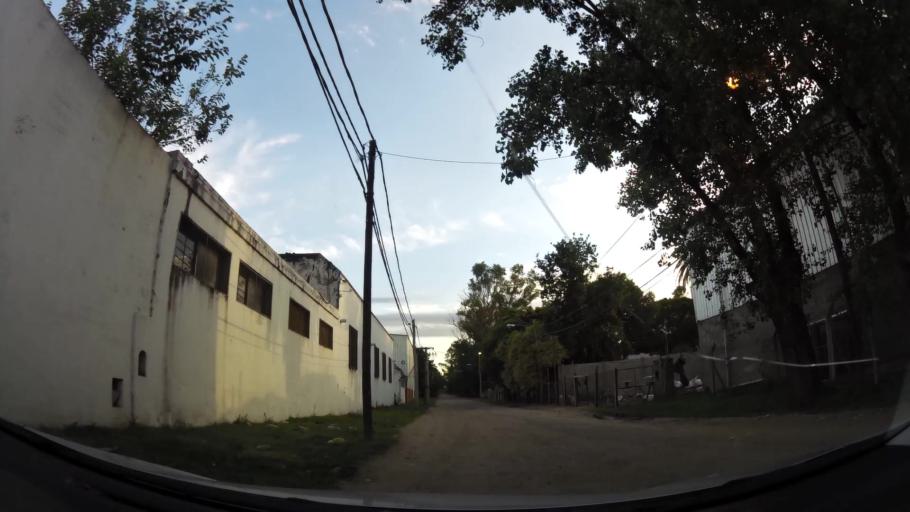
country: AR
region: Buenos Aires
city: Santa Catalina - Dique Lujan
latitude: -34.4504
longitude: -58.6629
